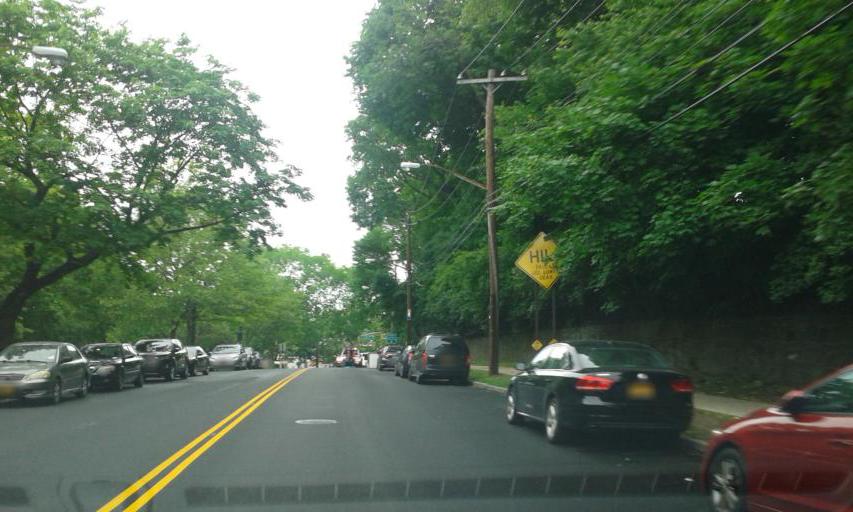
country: US
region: New Jersey
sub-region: Hudson County
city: Bayonne
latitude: 40.6289
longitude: -74.0901
